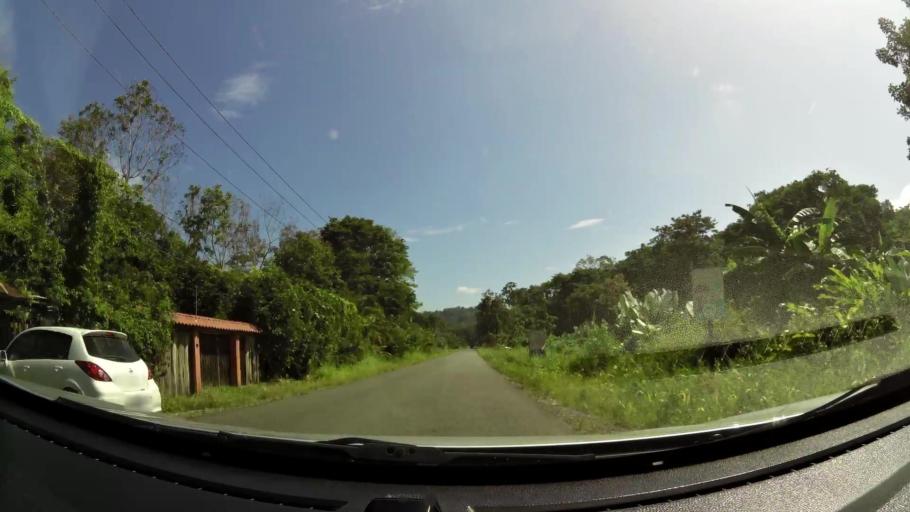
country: PA
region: Bocas del Toro
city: Barranco
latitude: 9.6522
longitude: -82.7945
